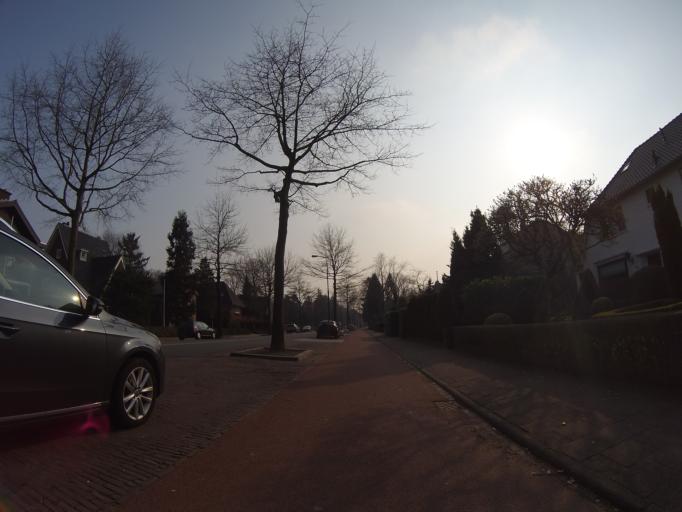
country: NL
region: Utrecht
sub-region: Gemeente Soest
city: Soest
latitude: 52.1614
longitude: 5.3084
